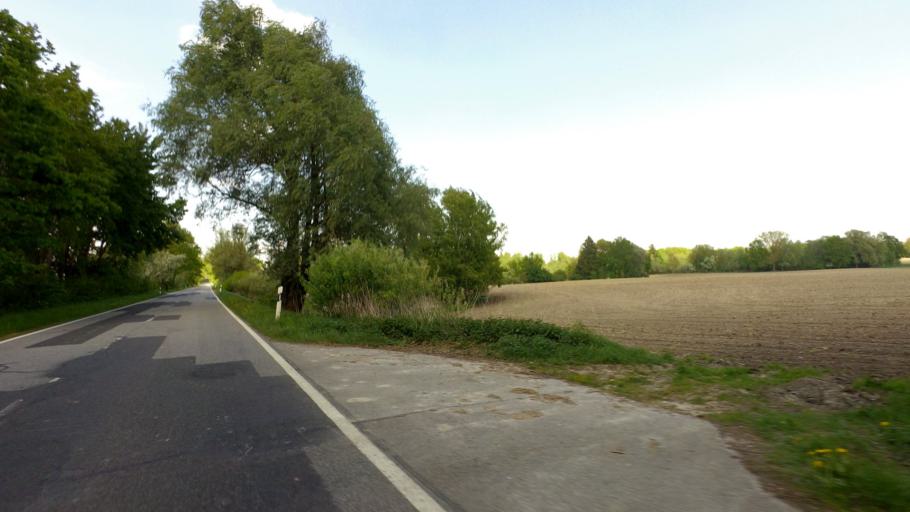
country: DE
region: Mecklenburg-Vorpommern
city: Mollenhagen
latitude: 53.5430
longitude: 12.9278
